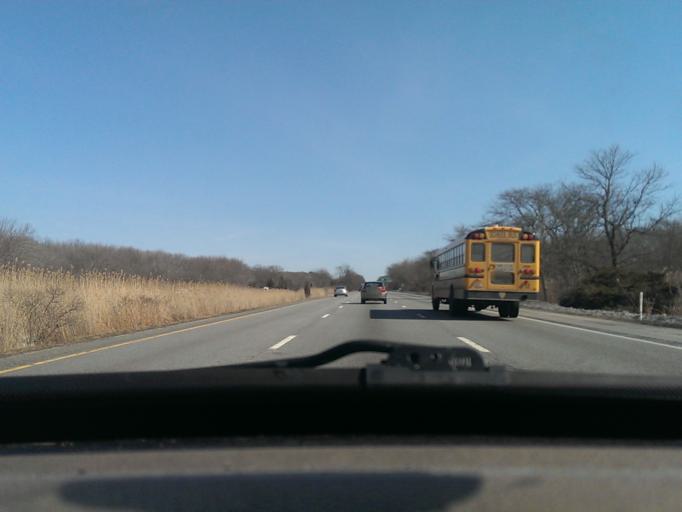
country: US
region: Rhode Island
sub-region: Bristol County
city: Warren
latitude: 41.7768
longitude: -71.2723
